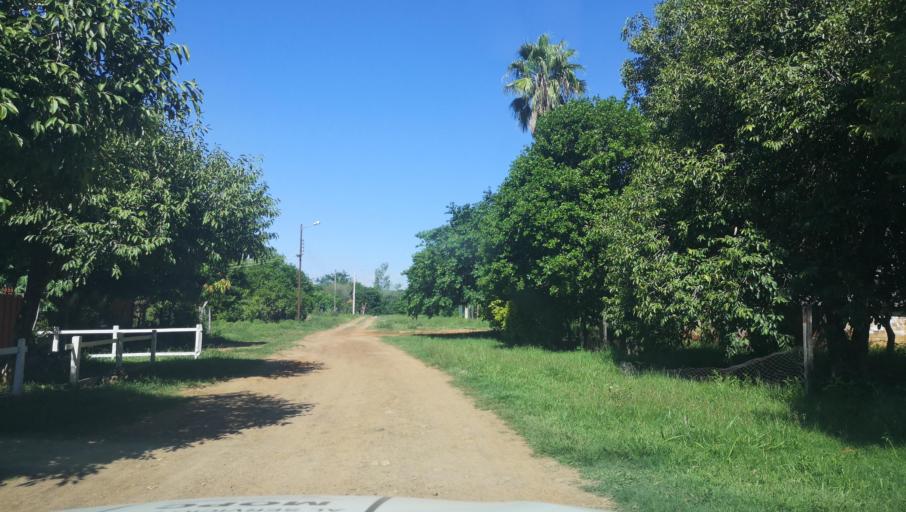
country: PY
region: Caaguazu
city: Carayao
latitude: -25.1944
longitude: -56.3974
